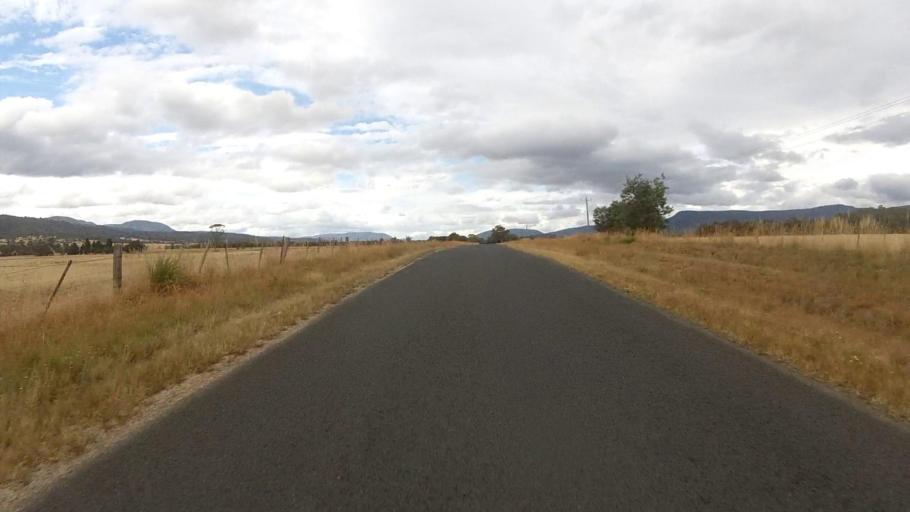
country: AU
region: Tasmania
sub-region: Northern Midlands
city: Evandale
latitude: -41.8237
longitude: 147.8193
